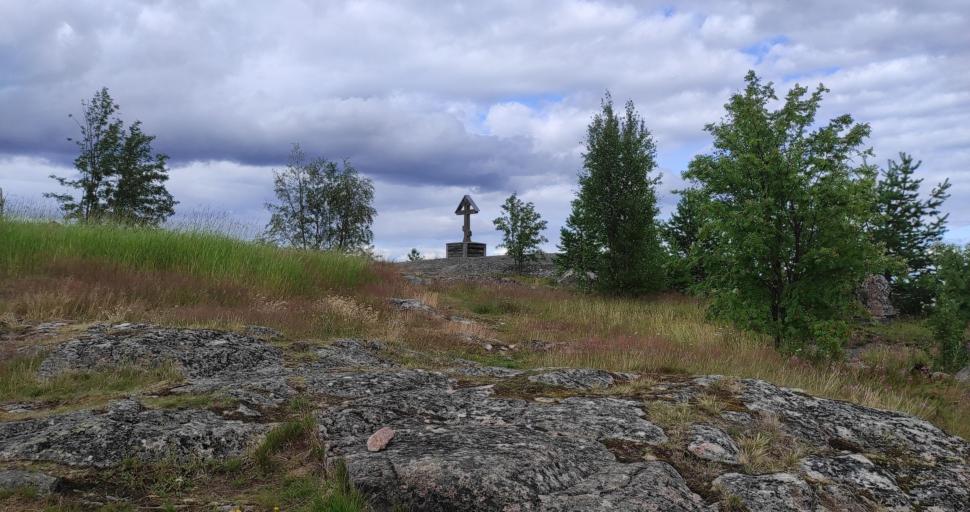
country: RU
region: Murmansk
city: Poyakonda
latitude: 66.6924
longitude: 32.8658
